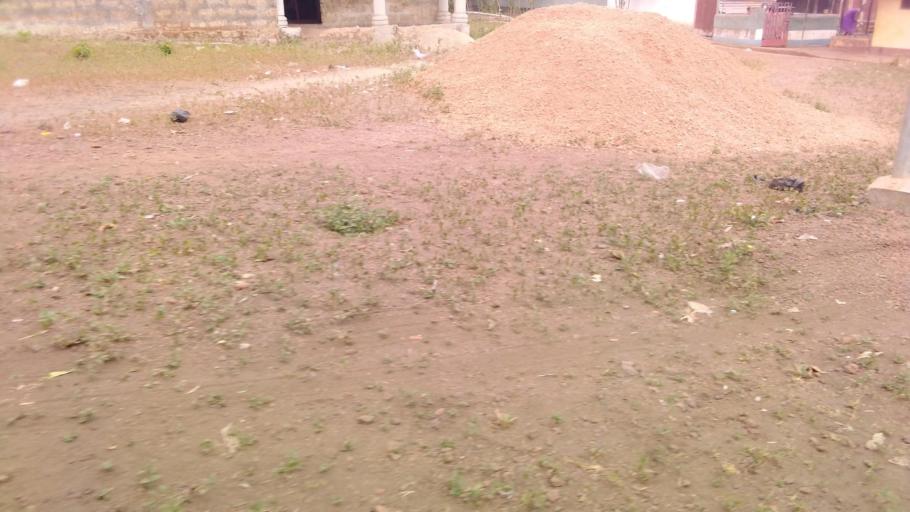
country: SL
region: Southern Province
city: Mogbwemo
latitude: 7.7876
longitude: -12.2942
